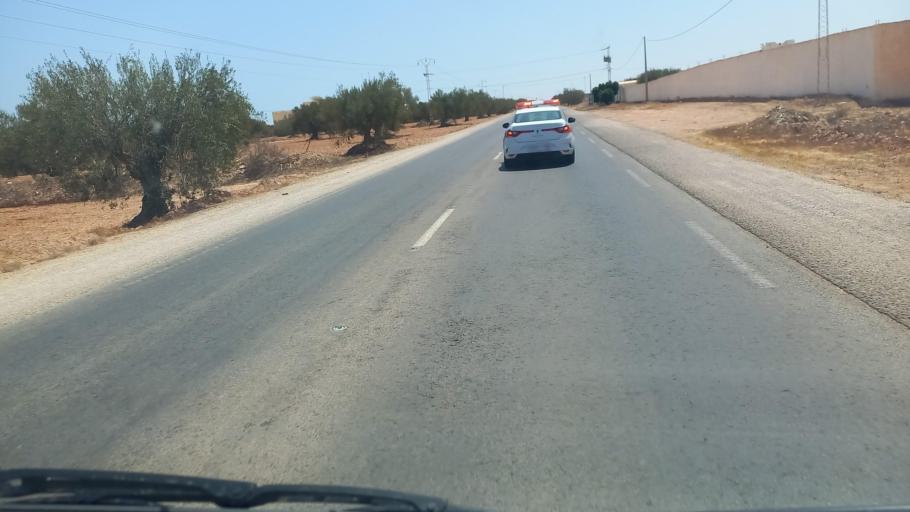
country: TN
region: Madanin
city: Zarzis
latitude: 33.5634
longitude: 11.0516
